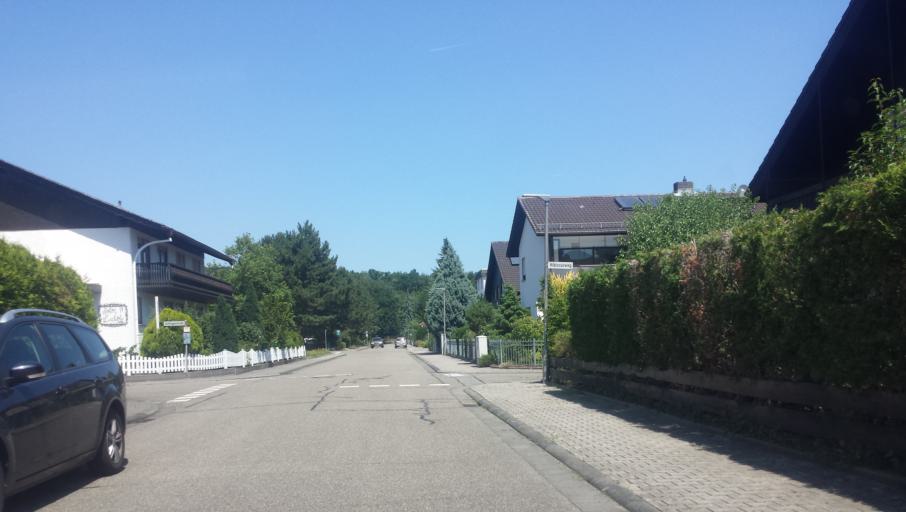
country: DE
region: Hesse
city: Lorsch
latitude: 49.6410
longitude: 8.5660
